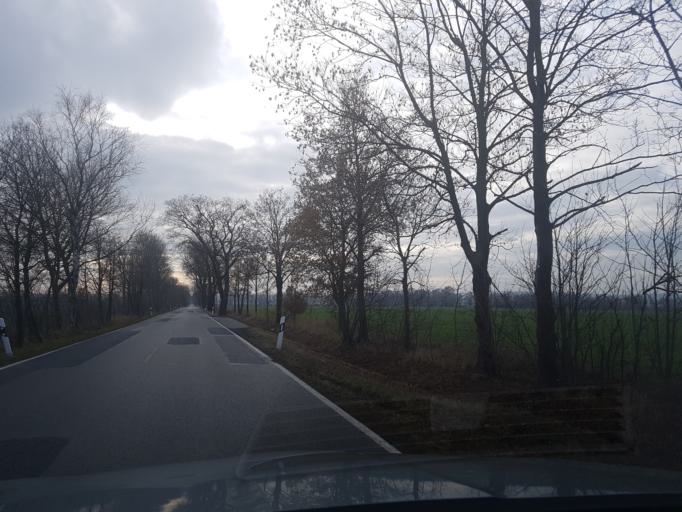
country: DE
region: Brandenburg
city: Hirschfeld
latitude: 51.4206
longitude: 13.6225
